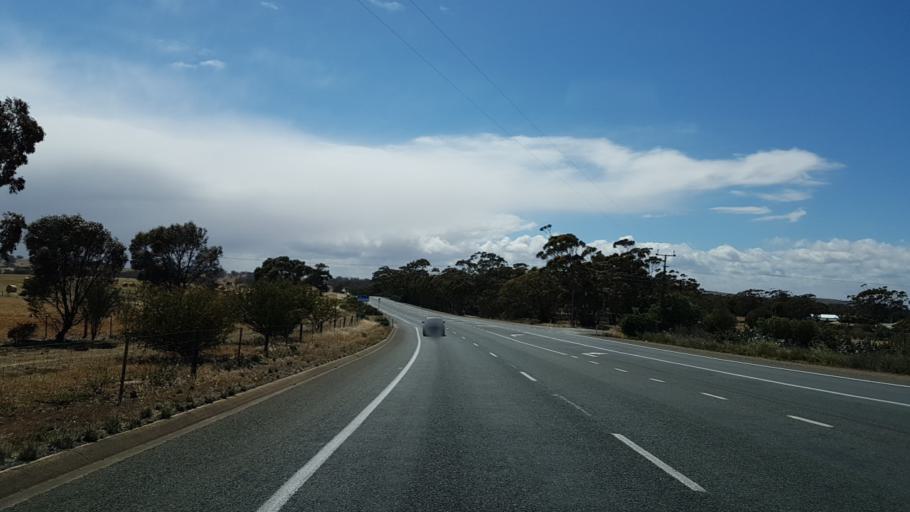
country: AU
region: South Australia
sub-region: Barossa
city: Angaston
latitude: -34.4051
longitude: 139.1460
